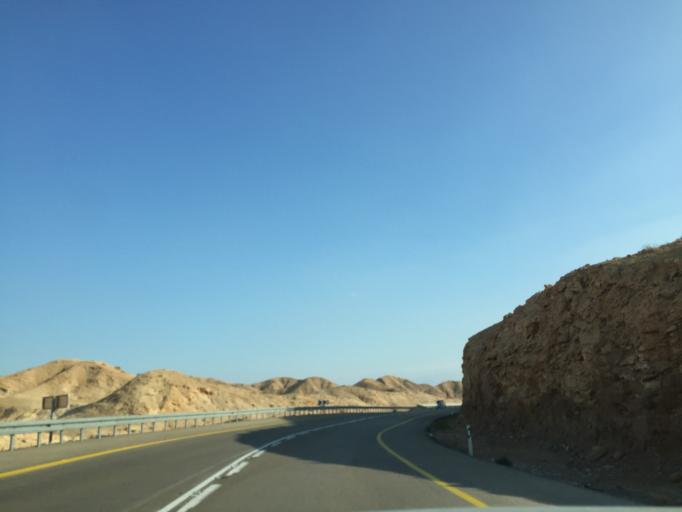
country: IL
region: Southern District
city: `En Boqeq
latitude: 31.1883
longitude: 35.2868
